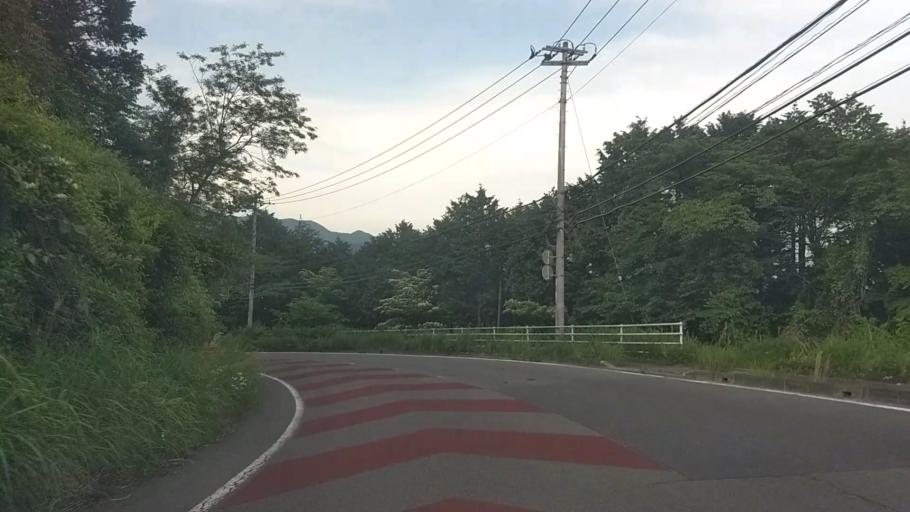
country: JP
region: Shizuoka
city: Gotemba
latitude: 35.3611
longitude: 138.9737
